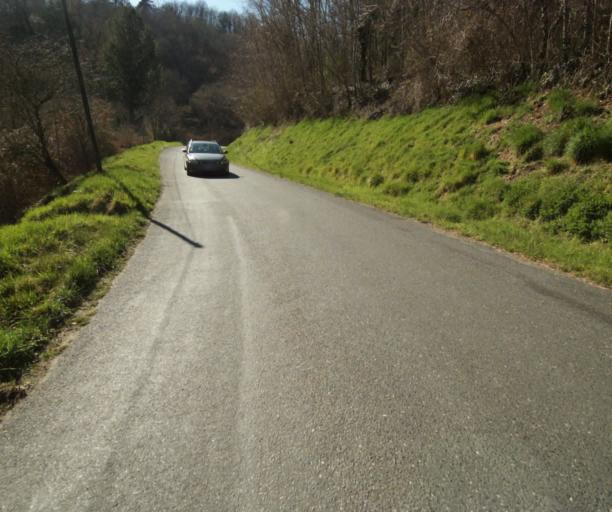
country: FR
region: Limousin
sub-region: Departement de la Correze
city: Tulle
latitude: 45.2745
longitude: 1.7373
